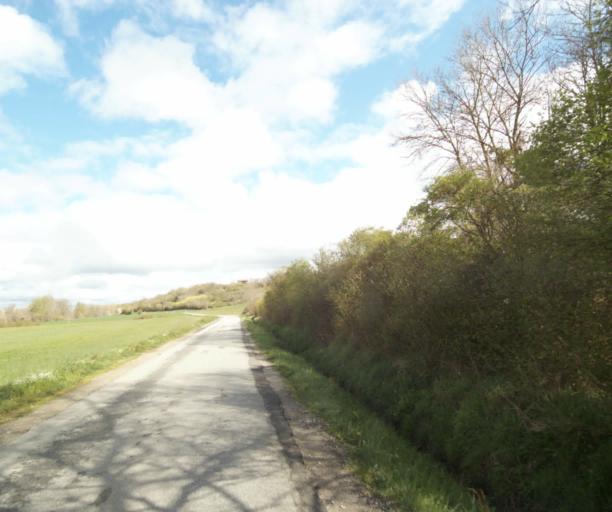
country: FR
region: Midi-Pyrenees
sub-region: Departement de l'Ariege
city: Saverdun
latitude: 43.2301
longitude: 1.5634
